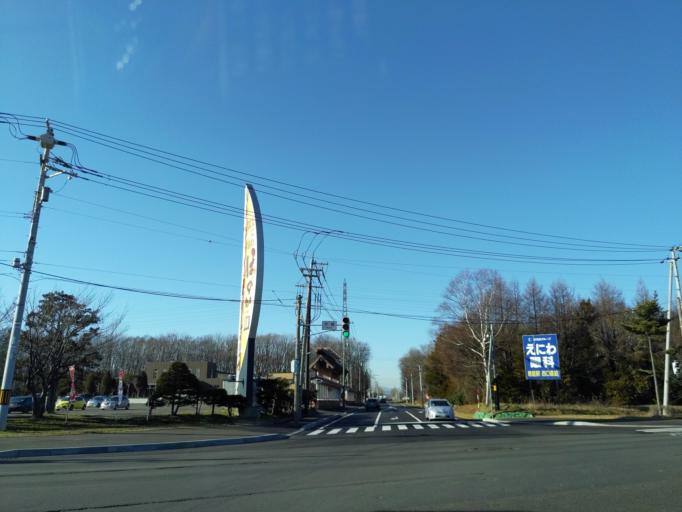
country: JP
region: Hokkaido
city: Chitose
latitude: 42.8771
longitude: 141.6083
